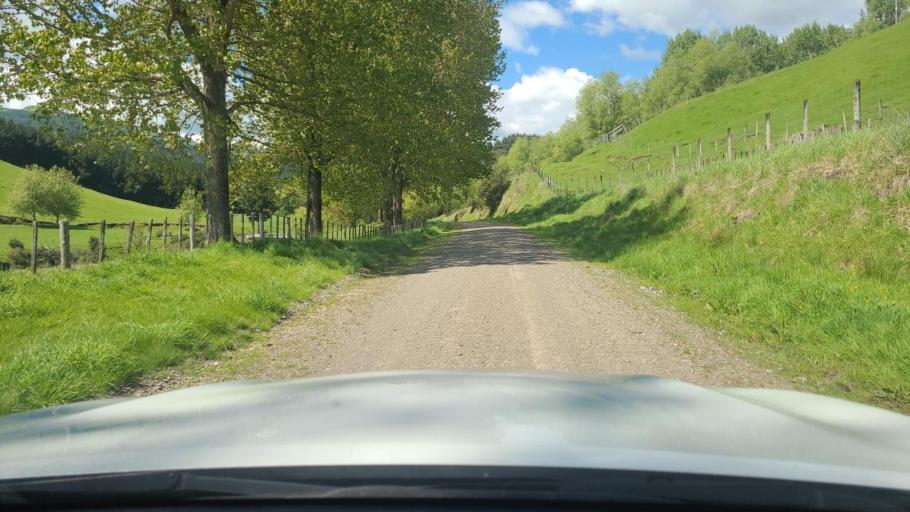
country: NZ
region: Hawke's Bay
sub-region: Napier City
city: Napier
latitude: -39.1690
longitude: 176.6580
